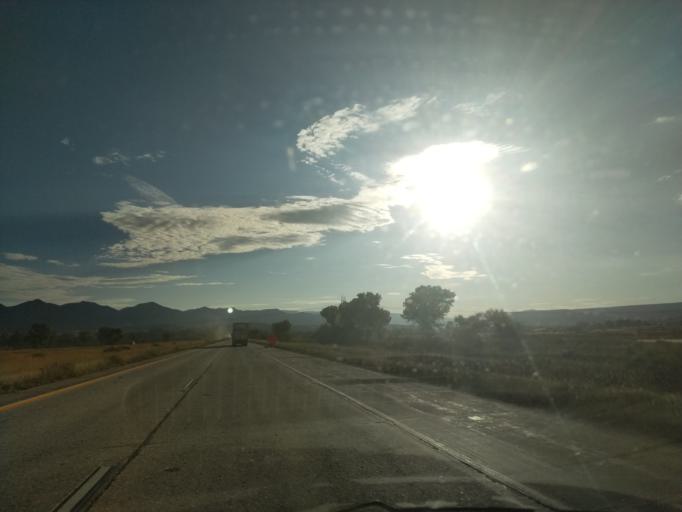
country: US
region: Colorado
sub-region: Garfield County
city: Silt
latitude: 39.5364
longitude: -107.6851
